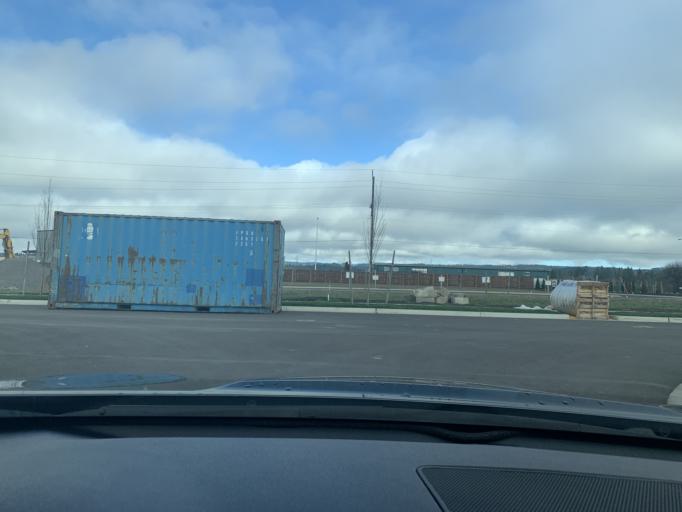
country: US
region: Oregon
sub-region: Washington County
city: North Plains
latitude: 45.5955
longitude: -122.9782
